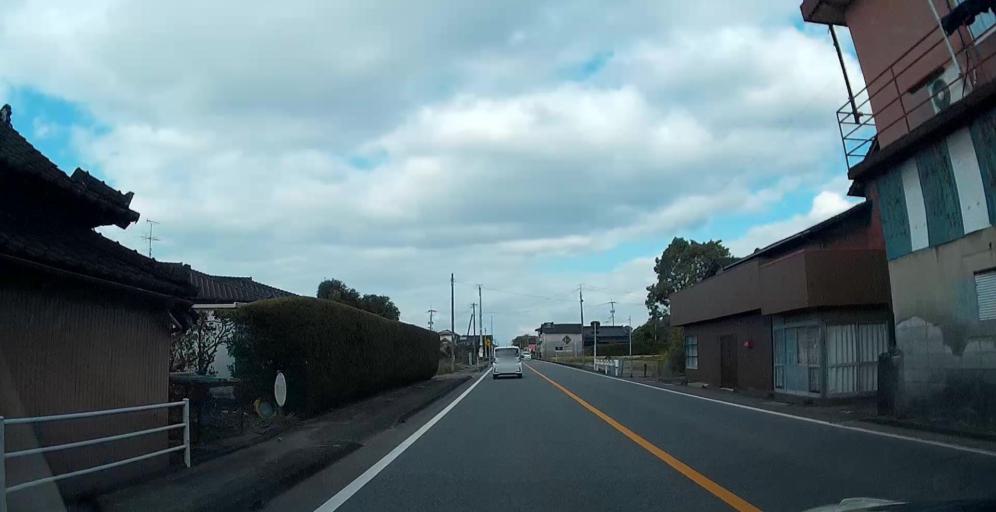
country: JP
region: Kumamoto
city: Yatsushiro
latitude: 32.4409
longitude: 130.5858
